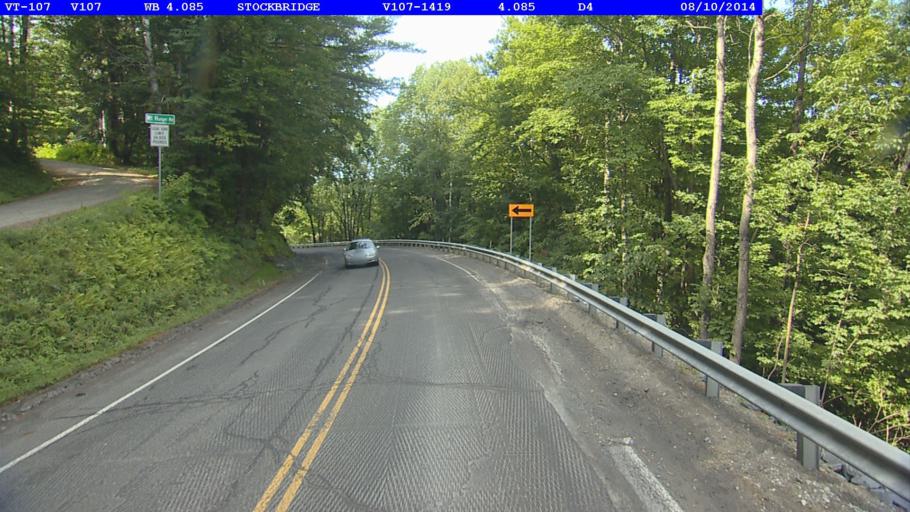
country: US
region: Vermont
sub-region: Orange County
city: Randolph
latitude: 43.7751
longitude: -72.7031
